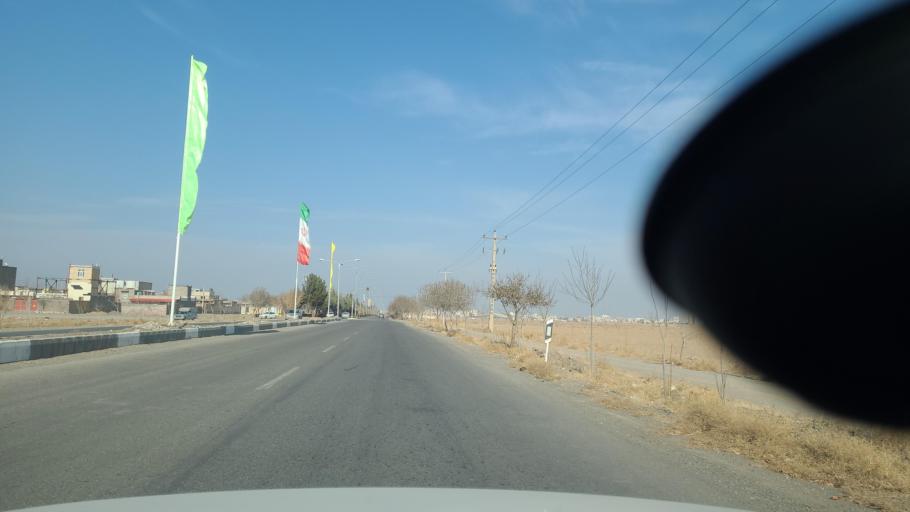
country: IR
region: Razavi Khorasan
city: Fariman
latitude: 35.6799
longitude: 59.8430
